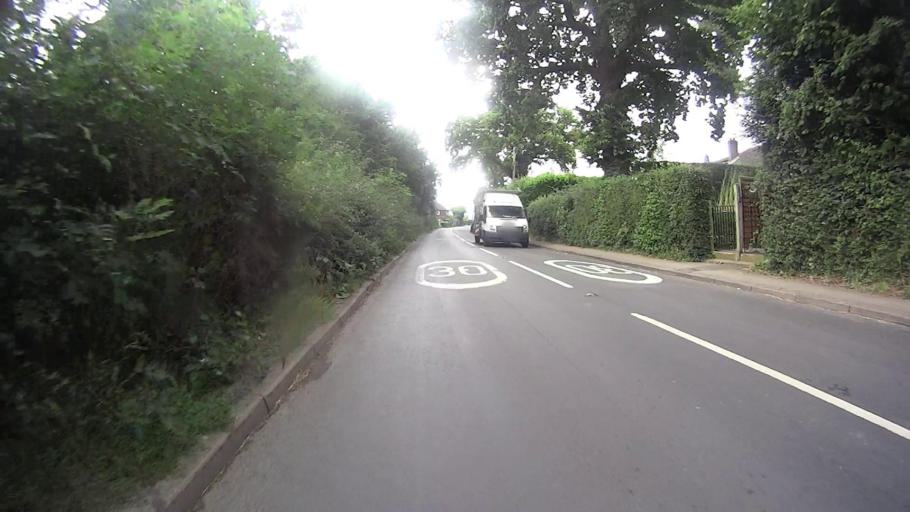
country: GB
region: England
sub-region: Surrey
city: Newdigate
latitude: 51.1670
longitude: -0.2901
